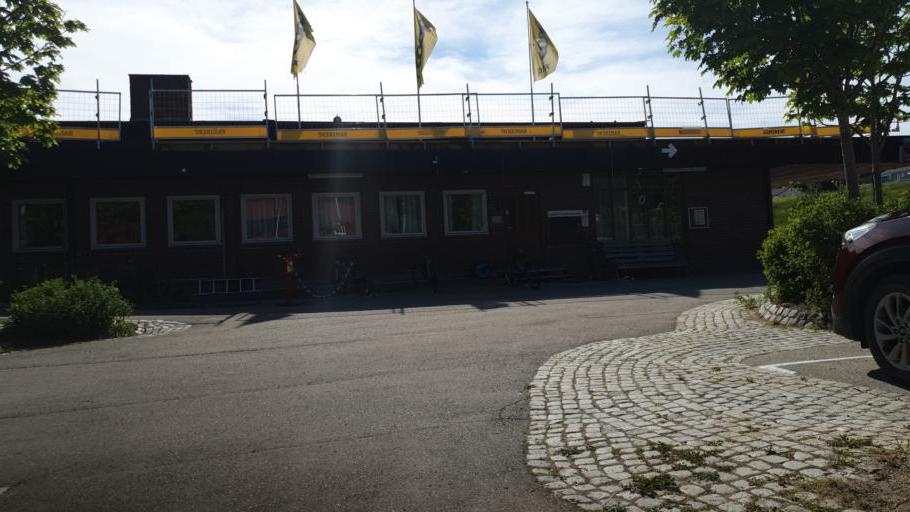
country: NO
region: Nord-Trondelag
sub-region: Leksvik
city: Leksvik
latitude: 63.6733
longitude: 10.6264
